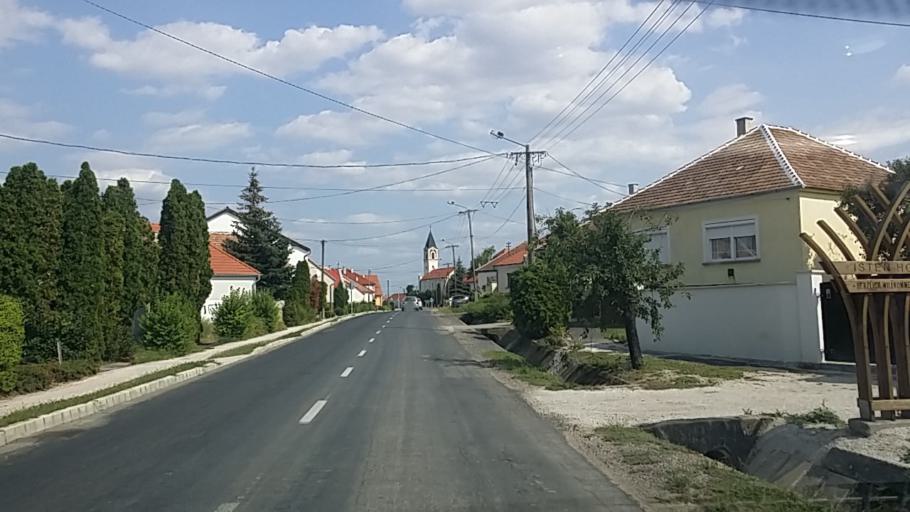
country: HU
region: Gyor-Moson-Sopron
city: Nagycenk
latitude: 47.6210
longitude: 16.7612
